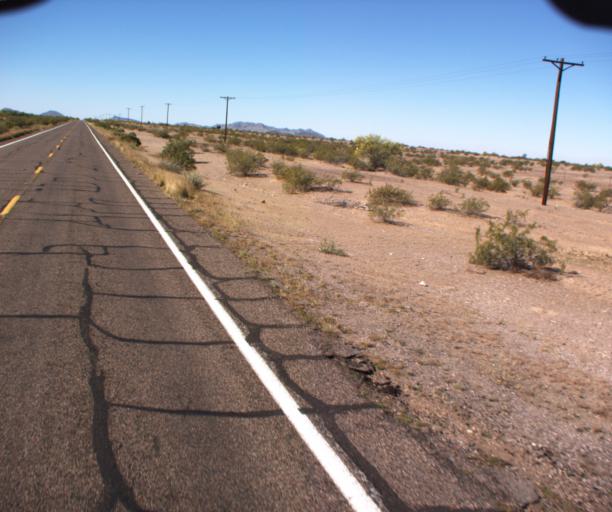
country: US
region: Arizona
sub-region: Maricopa County
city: Gila Bend
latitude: 32.8971
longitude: -112.7451
